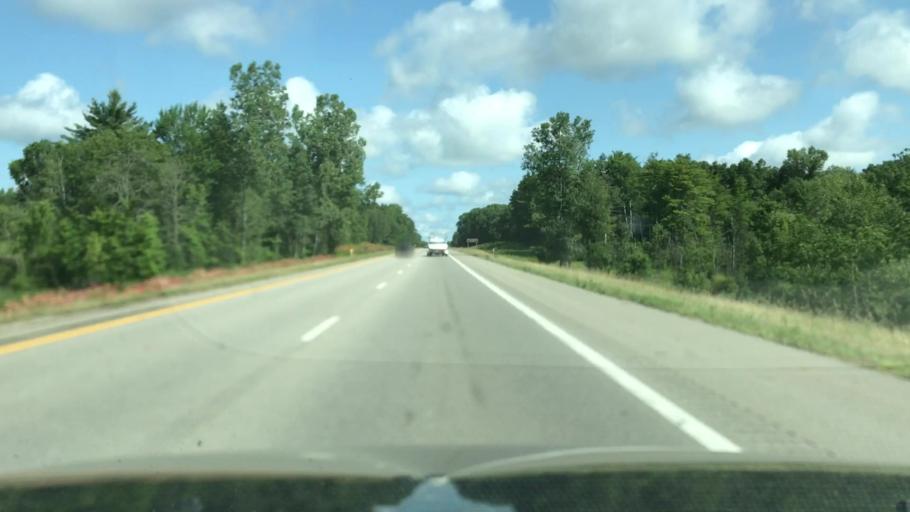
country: US
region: Michigan
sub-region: Montcalm County
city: Howard City
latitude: 43.4734
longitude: -85.4777
